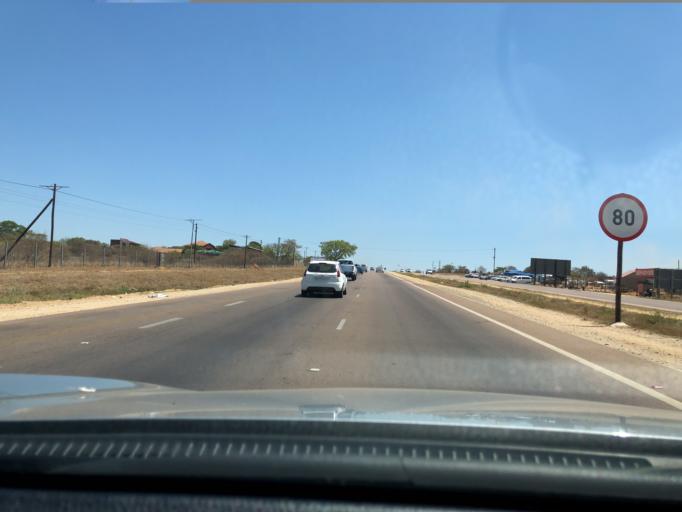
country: ZA
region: Limpopo
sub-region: Capricorn District Municipality
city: Polokwane
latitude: -23.8986
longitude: 29.5215
